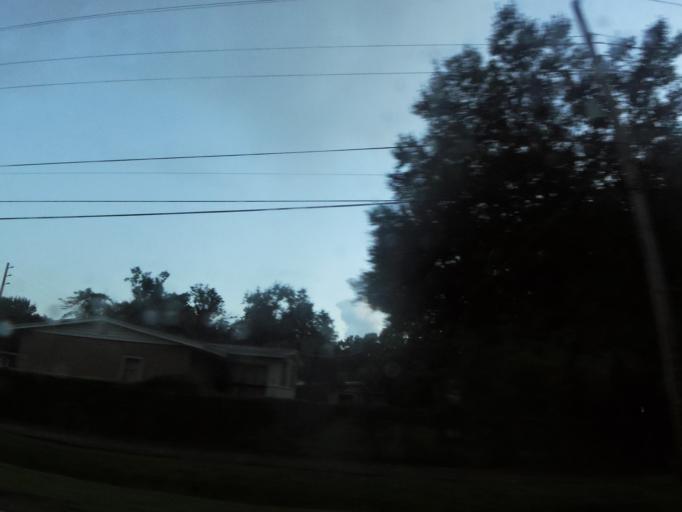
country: US
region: Florida
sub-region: Duval County
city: Jacksonville
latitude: 30.2458
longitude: -81.6162
